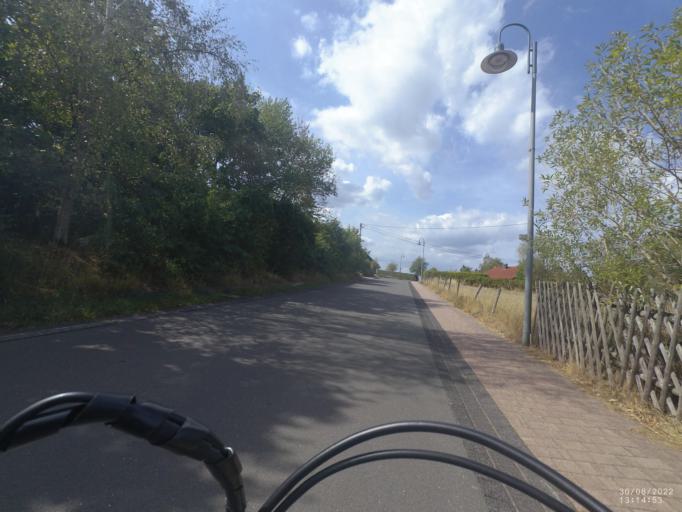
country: DE
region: Rheinland-Pfalz
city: Scheid
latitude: 50.3597
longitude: 6.4206
